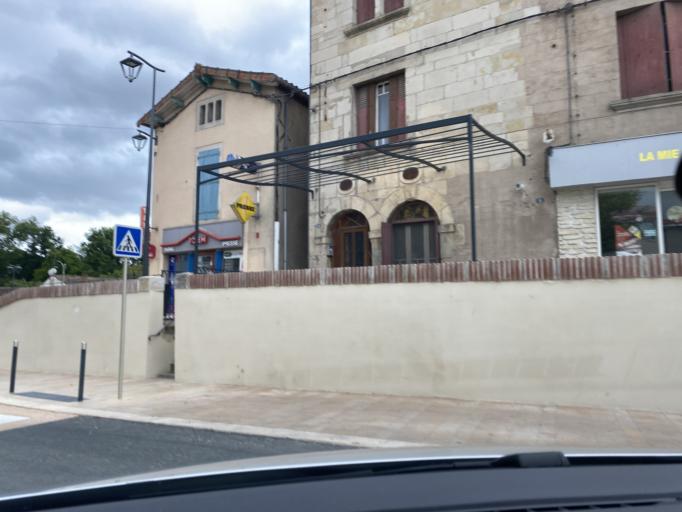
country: FR
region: Midi-Pyrenees
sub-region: Departement du Tarn
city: Saix
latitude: 43.5817
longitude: 2.1839
